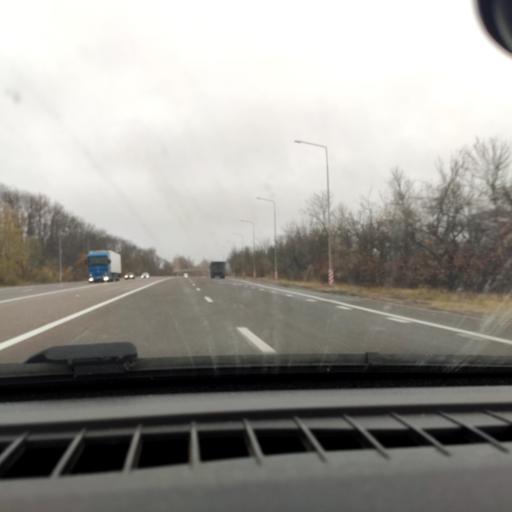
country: RU
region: Voronezj
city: Kolodeznyy
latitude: 51.3356
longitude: 39.0247
